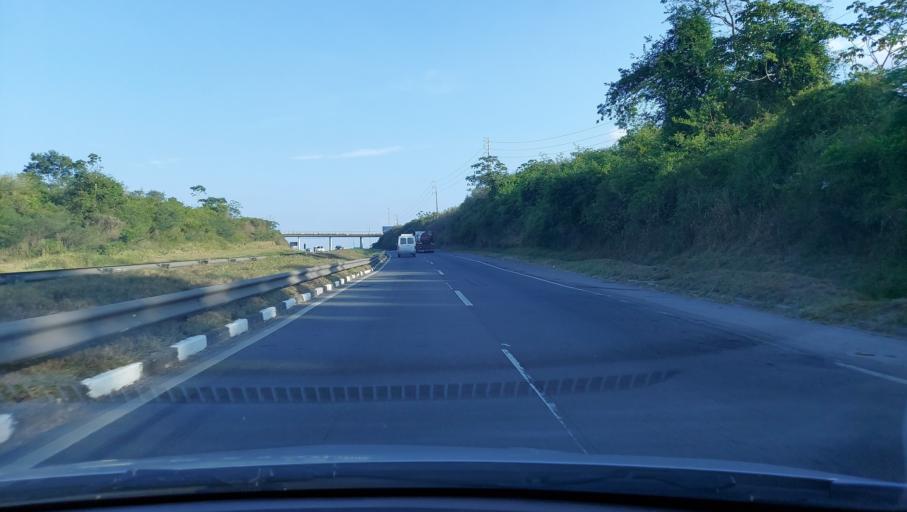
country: BR
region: Bahia
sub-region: Conceicao Do Jacuipe
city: Conceicao do Jacuipe
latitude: -12.3581
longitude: -38.8277
